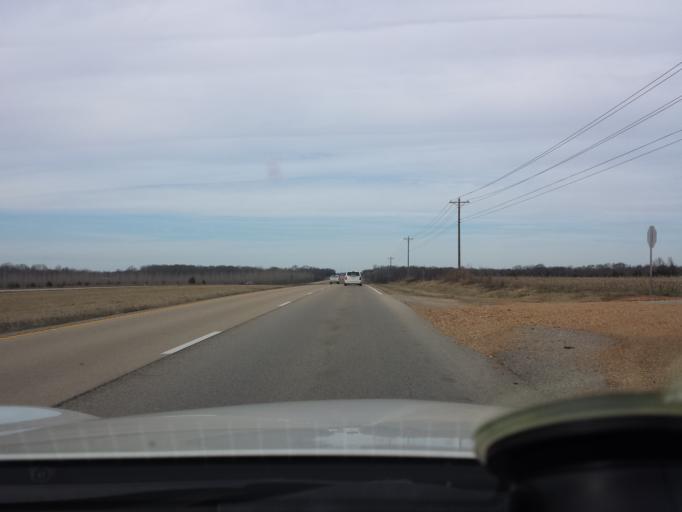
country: US
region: Mississippi
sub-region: Clay County
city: West Point
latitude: 33.7403
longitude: -88.6794
